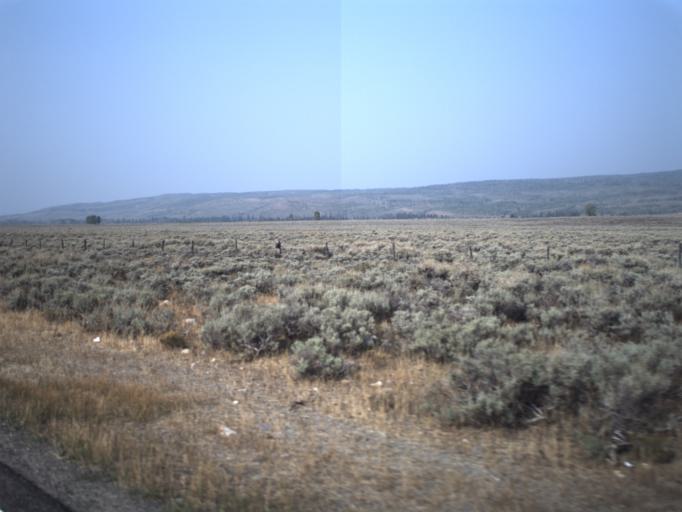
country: US
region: Wyoming
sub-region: Uinta County
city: Evanston
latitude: 40.9493
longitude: -110.8405
